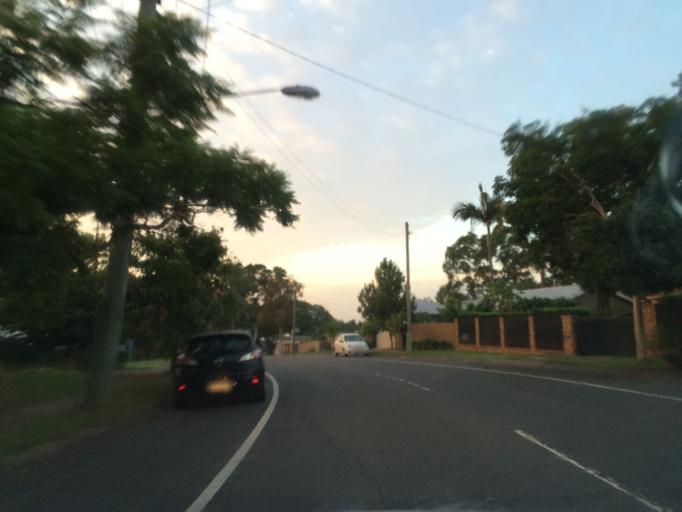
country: AU
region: Queensland
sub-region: Brisbane
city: Kenmore Hills
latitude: -27.5034
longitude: 152.9504
